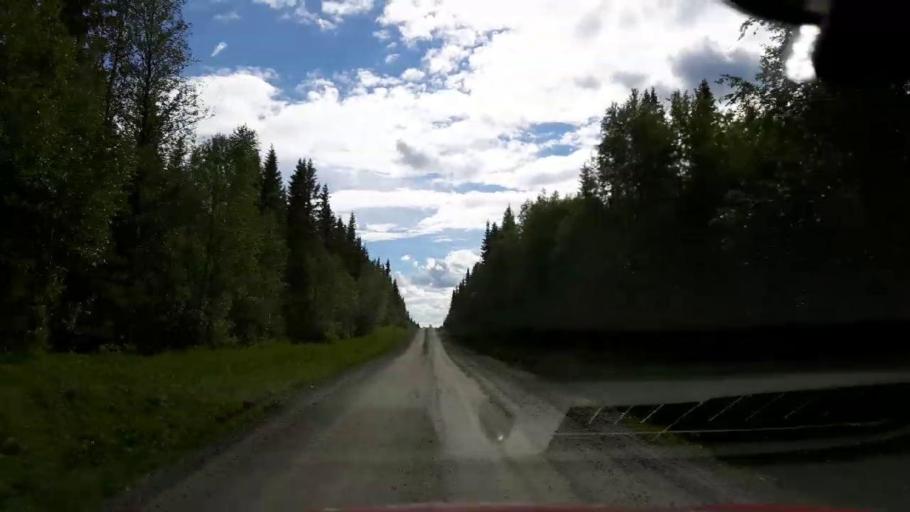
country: SE
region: Jaemtland
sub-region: Krokoms Kommun
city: Valla
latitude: 63.8902
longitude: 14.1575
